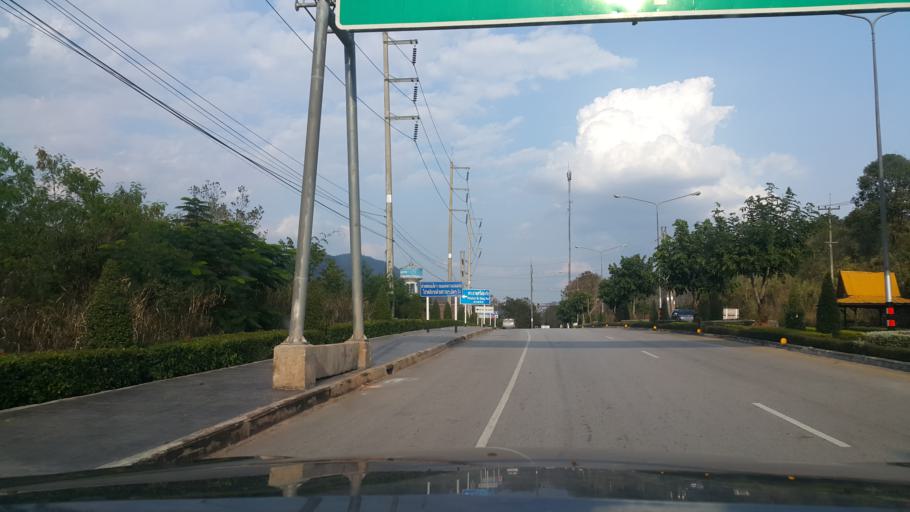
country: TH
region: Loei
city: Dan Sai
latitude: 17.2685
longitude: 101.1428
